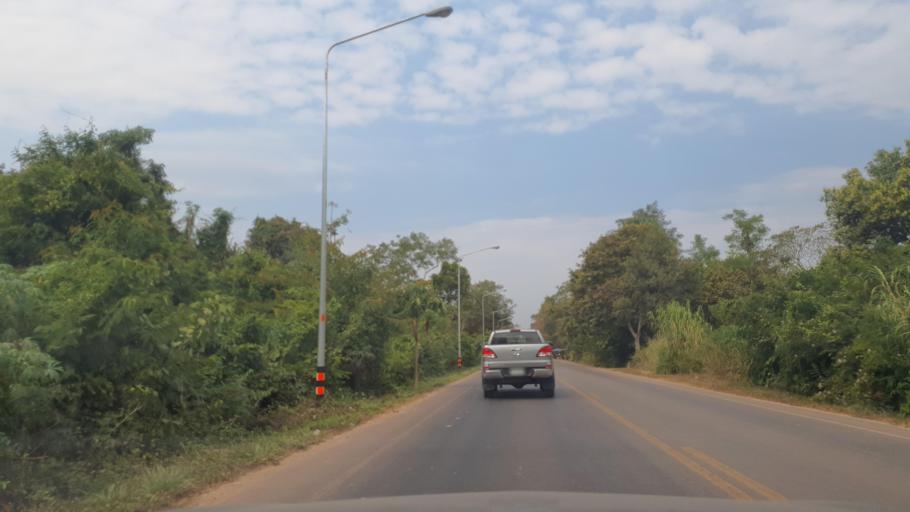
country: TH
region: Changwat Bueng Kan
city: Si Wilai
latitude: 18.2778
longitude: 103.8308
